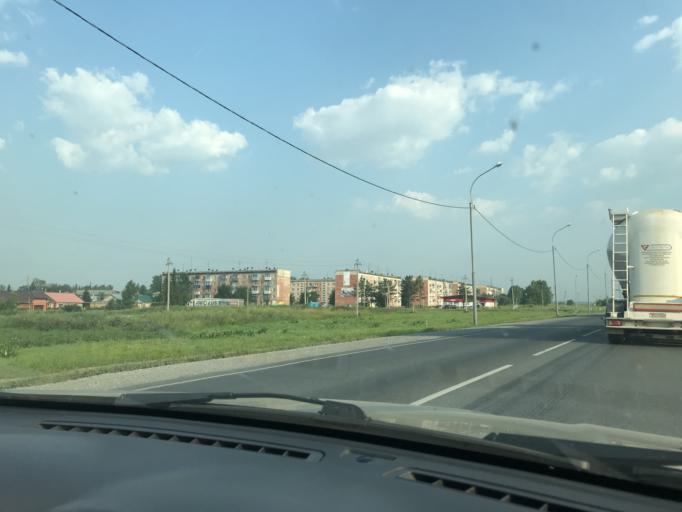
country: RU
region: Novosibirsk
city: Linevo
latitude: 54.5097
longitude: 83.3319
